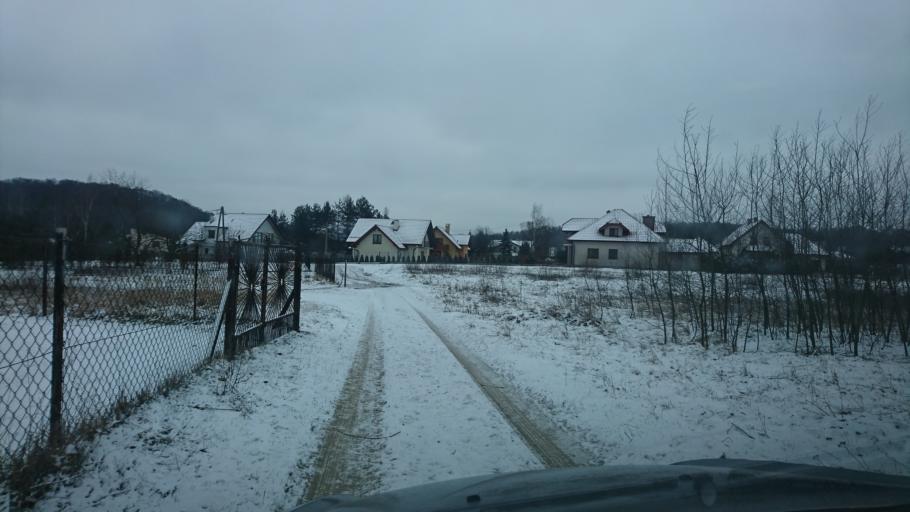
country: PL
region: Lesser Poland Voivodeship
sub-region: Powiat krakowski
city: Ochojno
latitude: 50.0046
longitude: 20.0013
